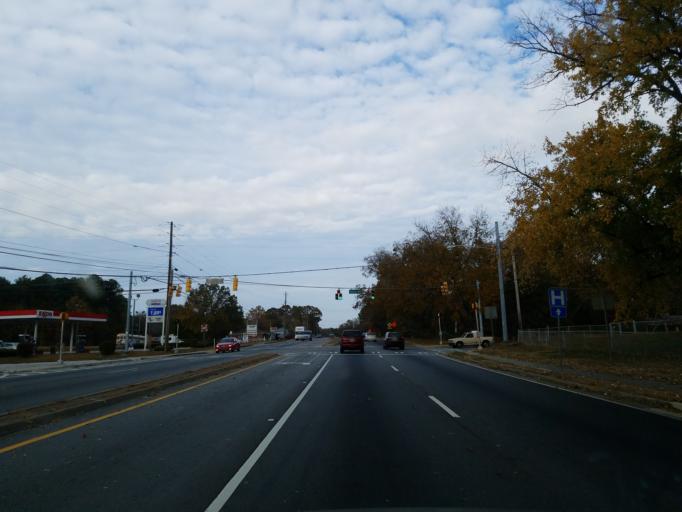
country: US
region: Georgia
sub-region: Cobb County
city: Mableton
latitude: 33.8400
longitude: -84.6108
